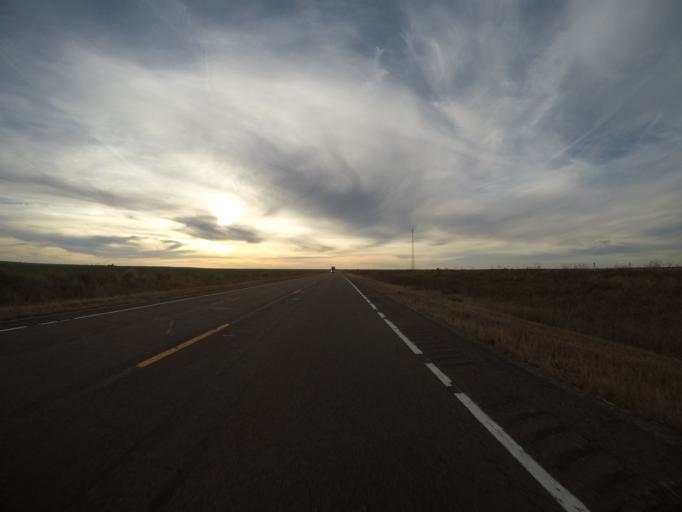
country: US
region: Colorado
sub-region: Yuma County
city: Yuma
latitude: 39.6700
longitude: -102.9373
